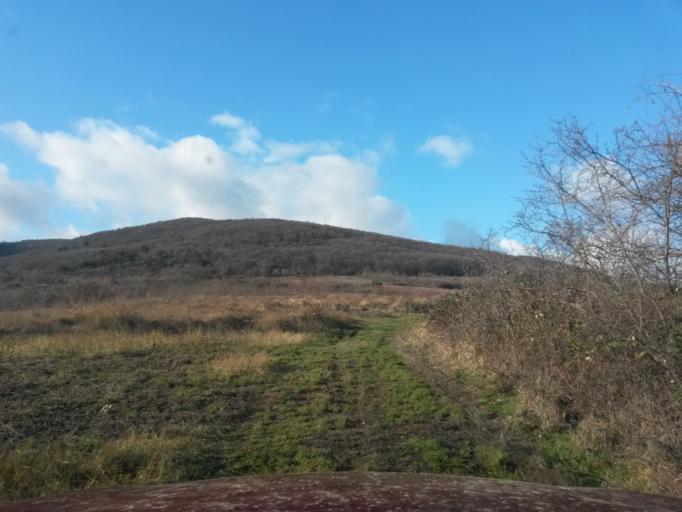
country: HU
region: Borsod-Abauj-Zemplen
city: Sarospatak
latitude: 48.3323
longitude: 21.5184
